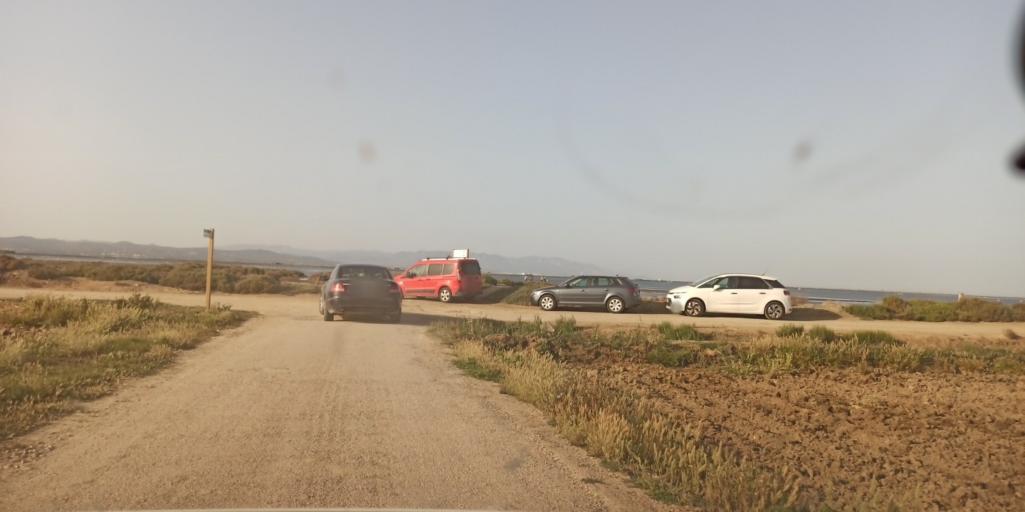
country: ES
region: Catalonia
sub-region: Provincia de Tarragona
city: Deltebre
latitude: 40.7627
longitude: 0.7545
